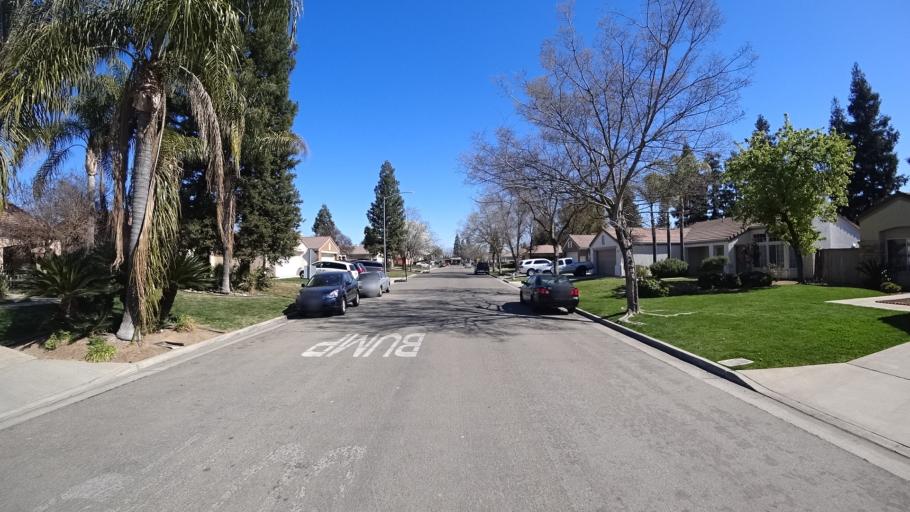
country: US
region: California
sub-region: Fresno County
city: Clovis
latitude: 36.8474
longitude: -119.7419
